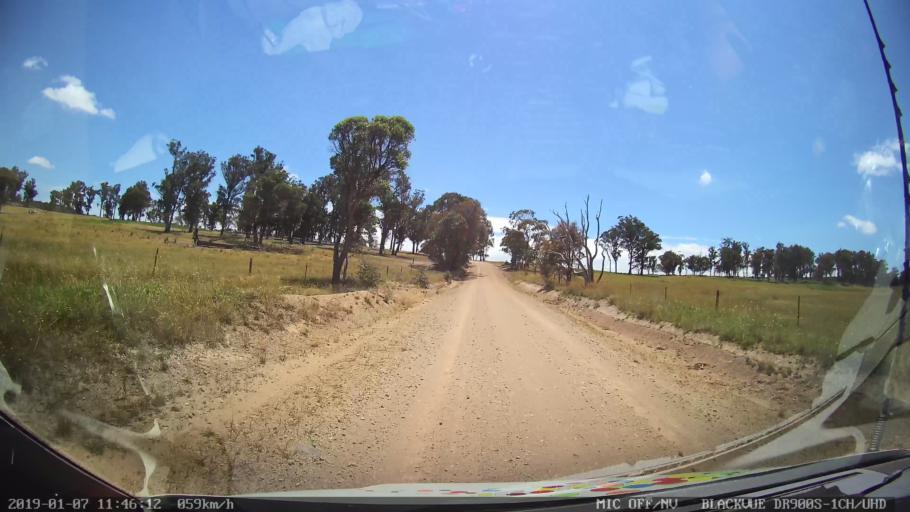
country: AU
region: New South Wales
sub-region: Guyra
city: Guyra
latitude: -30.3435
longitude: 151.6118
